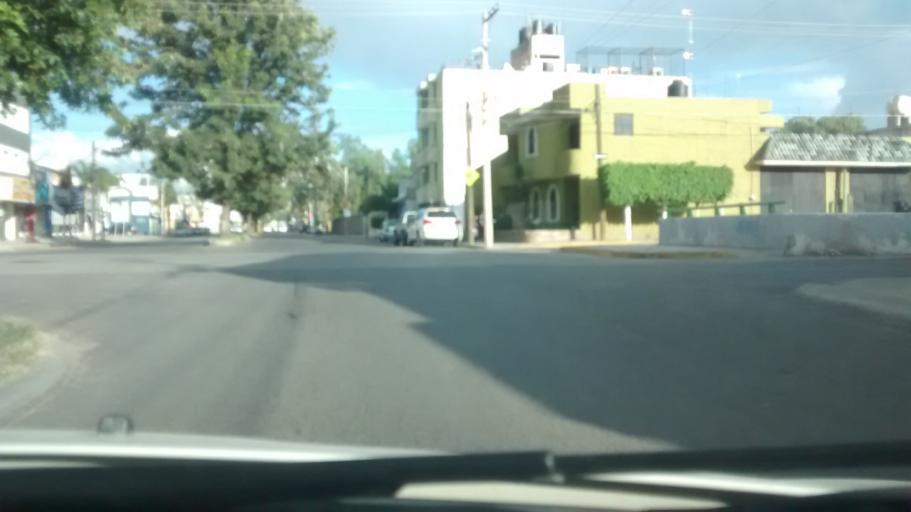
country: MX
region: Guanajuato
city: Leon
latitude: 21.0997
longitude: -101.6430
